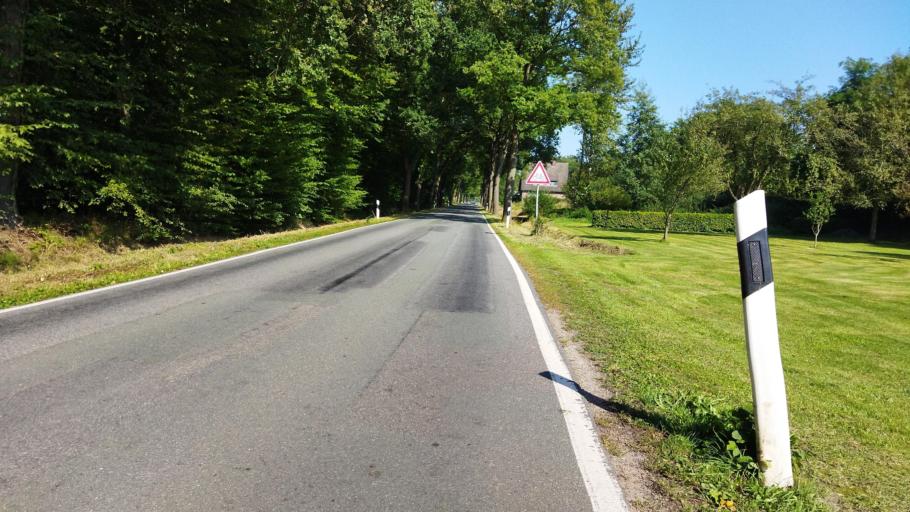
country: DE
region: Lower Saxony
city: Hasbergen
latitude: 52.2405
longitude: 7.9389
